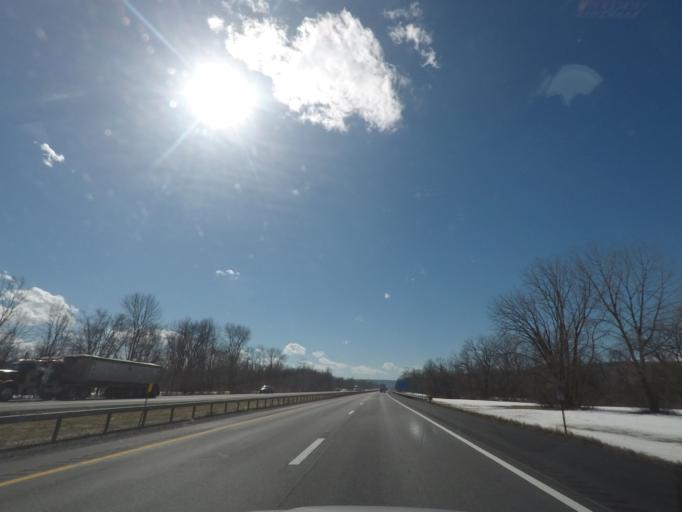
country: US
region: New York
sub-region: Montgomery County
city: Fonda
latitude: 42.9281
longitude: -74.4219
